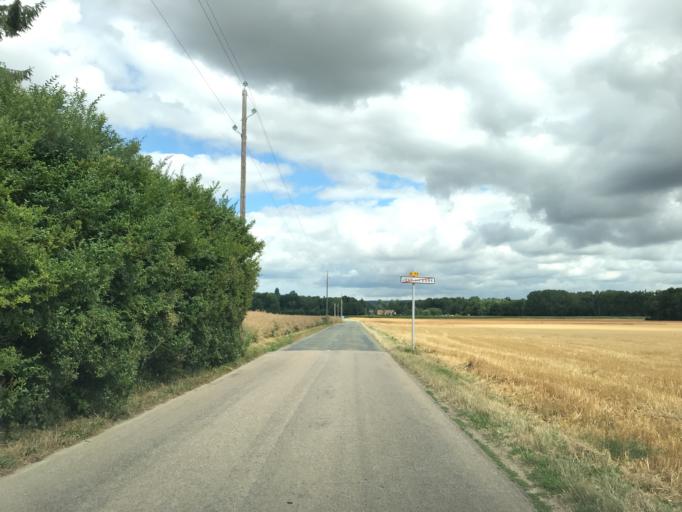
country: FR
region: Haute-Normandie
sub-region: Departement de l'Eure
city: Houlbec-Cocherel
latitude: 49.0547
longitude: 1.3001
